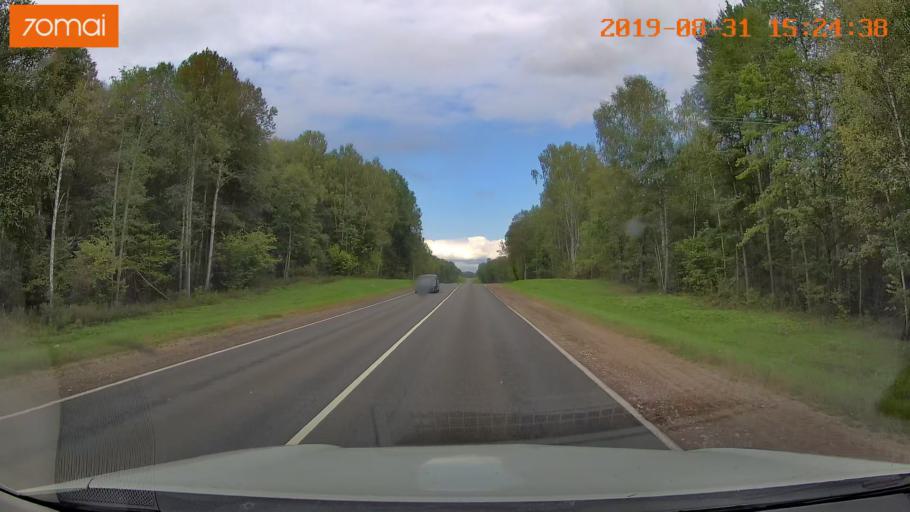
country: RU
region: Kaluga
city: Baryatino
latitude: 54.5303
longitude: 34.5075
